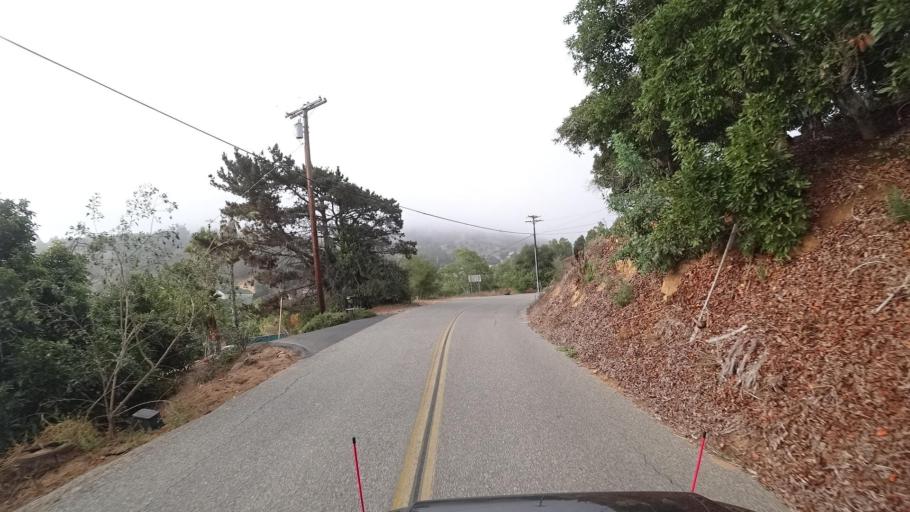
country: US
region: California
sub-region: San Diego County
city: Rainbow
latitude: 33.3421
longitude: -117.1722
